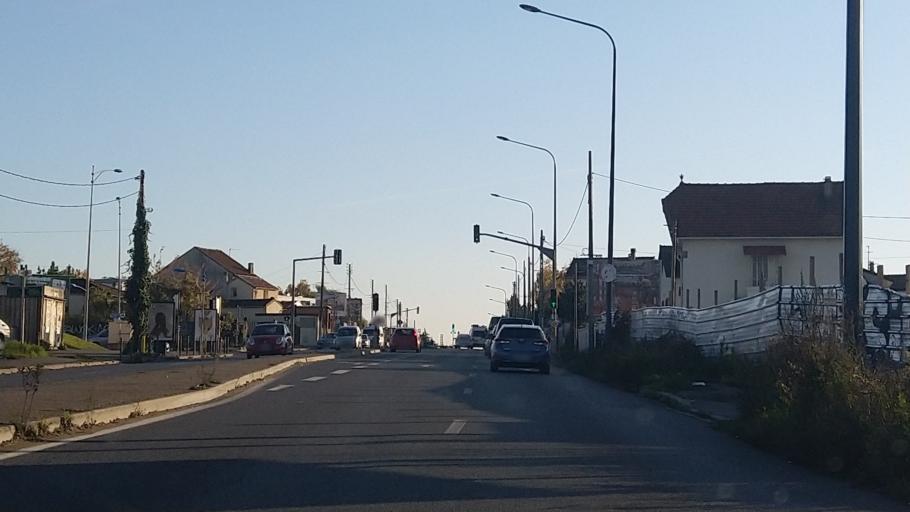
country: FR
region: Ile-de-France
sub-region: Departement de Seine-Saint-Denis
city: Pierrefitte-sur-Seine
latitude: 48.9796
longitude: 2.3638
